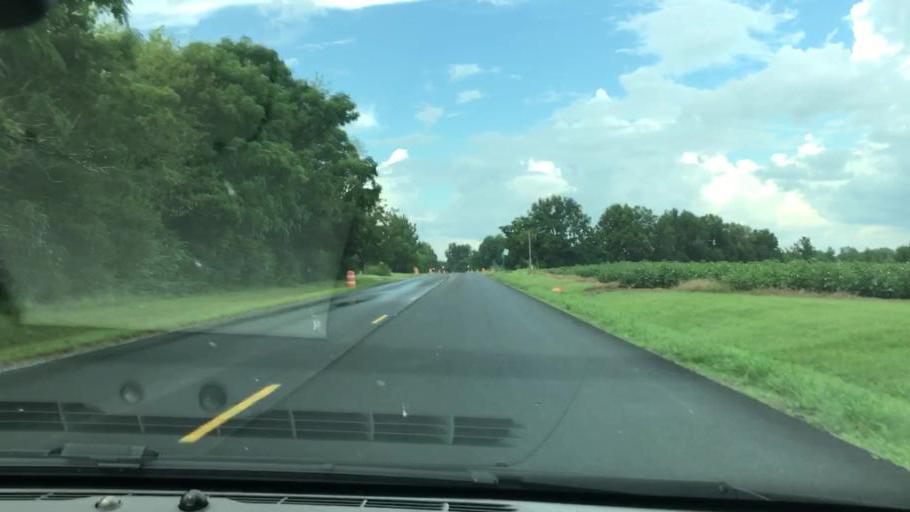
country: US
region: Georgia
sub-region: Early County
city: Blakely
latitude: 31.3925
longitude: -84.9469
